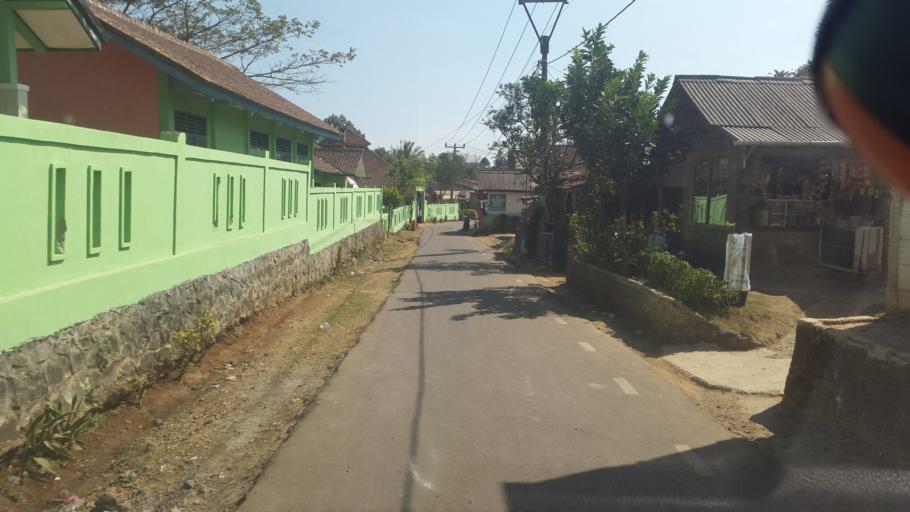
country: ID
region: West Java
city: Cicurug
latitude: -6.8533
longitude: 106.6971
